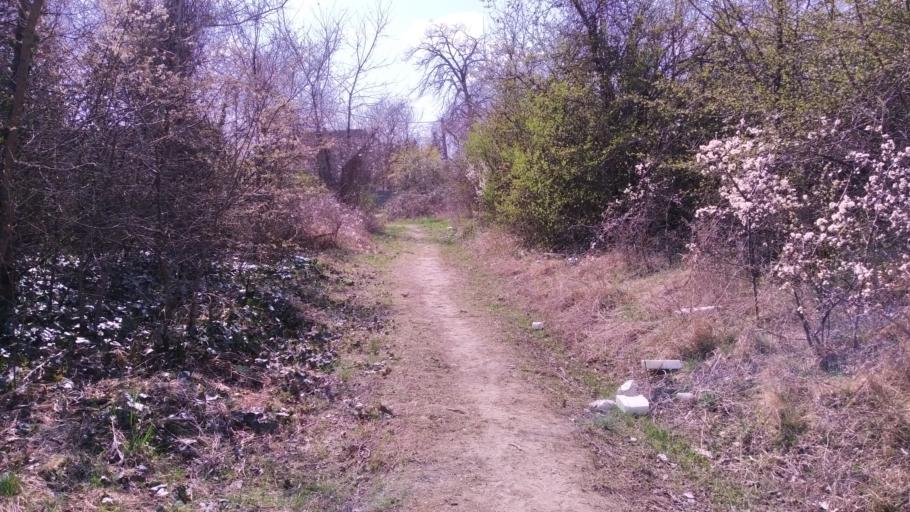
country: HU
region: Pest
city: Budakalasz
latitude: 47.6128
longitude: 19.0443
